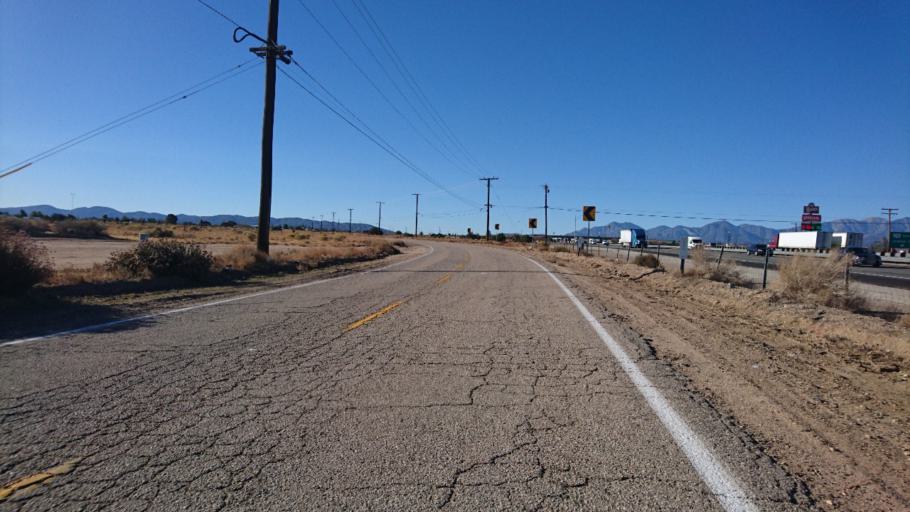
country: US
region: California
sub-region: San Bernardino County
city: Oak Hills
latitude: 34.4106
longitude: -117.3926
